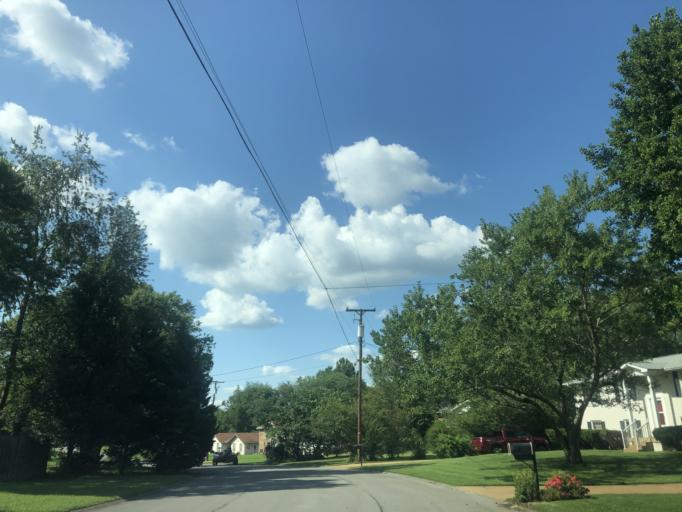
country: US
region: Tennessee
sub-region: Davidson County
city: Lakewood
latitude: 36.2069
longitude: -86.5986
